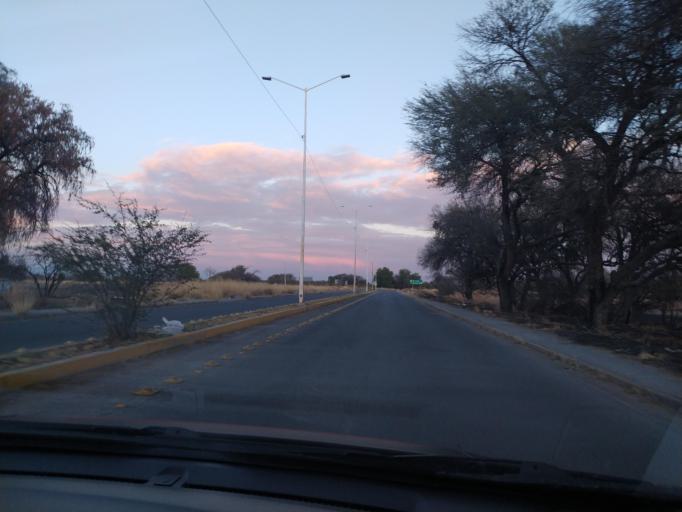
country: MX
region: Guanajuato
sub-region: San Francisco del Rincon
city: Fraccionamiento la Mezquitera
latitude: 21.0117
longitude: -101.8307
